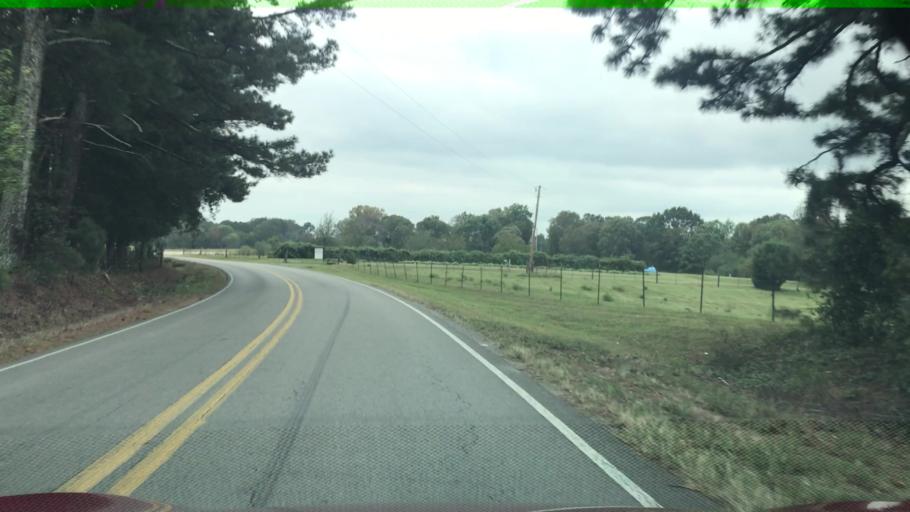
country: US
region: Alabama
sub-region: Cullman County
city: Good Hope
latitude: 34.0990
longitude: -87.0414
